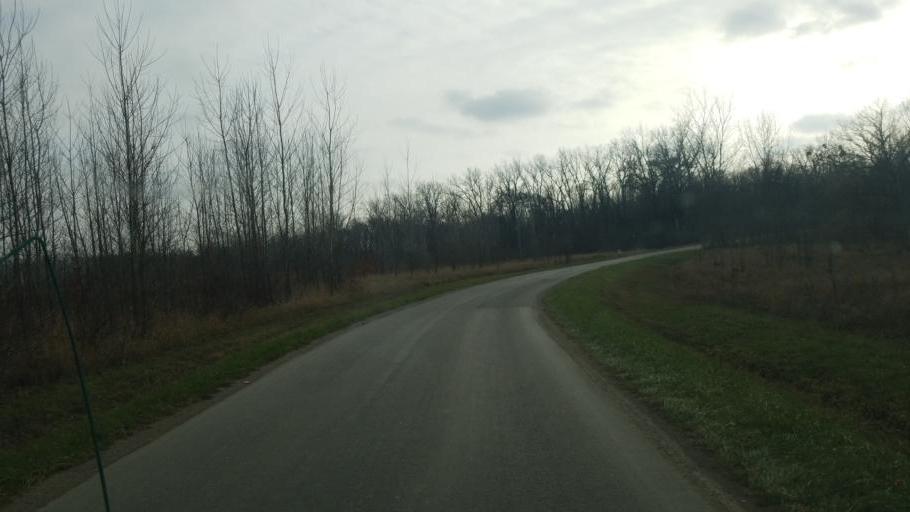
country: US
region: Indiana
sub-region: Adams County
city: Geneva
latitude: 40.6181
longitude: -84.9636
